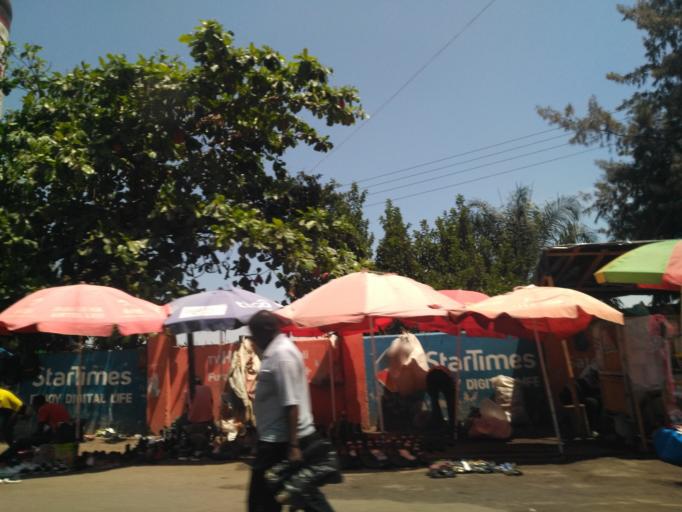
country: TZ
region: Mwanza
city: Mwanza
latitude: -2.5224
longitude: 32.9039
